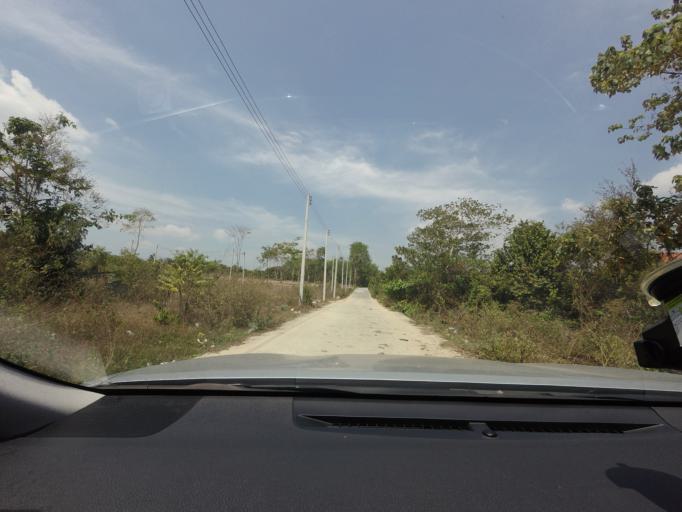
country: TH
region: Narathiwat
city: Rueso
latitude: 6.3780
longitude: 101.5080
